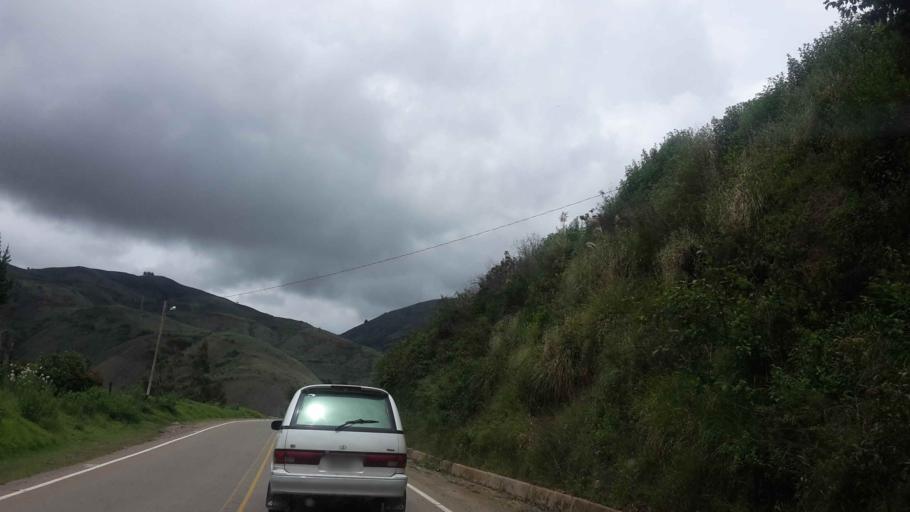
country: BO
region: Cochabamba
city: Totora
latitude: -17.5133
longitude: -65.3964
